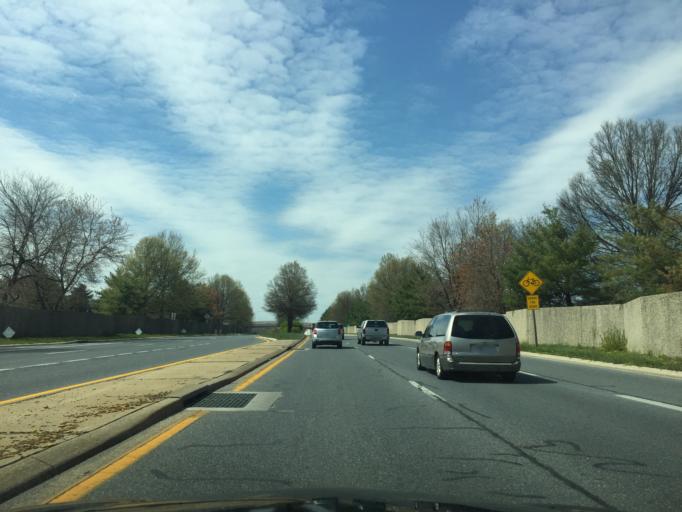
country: US
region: Maryland
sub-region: Baltimore County
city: Middle River
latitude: 39.3028
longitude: -76.4437
